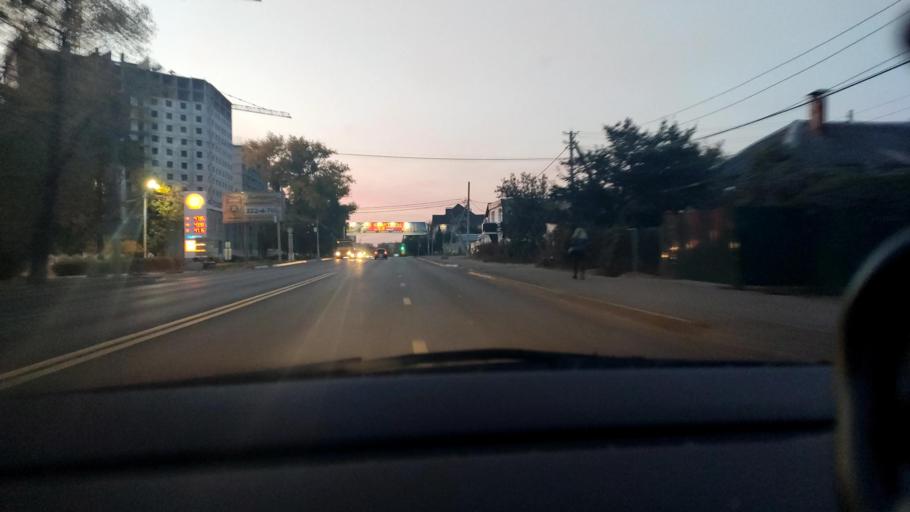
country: RU
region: Voronezj
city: Voronezh
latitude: 51.6984
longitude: 39.1965
